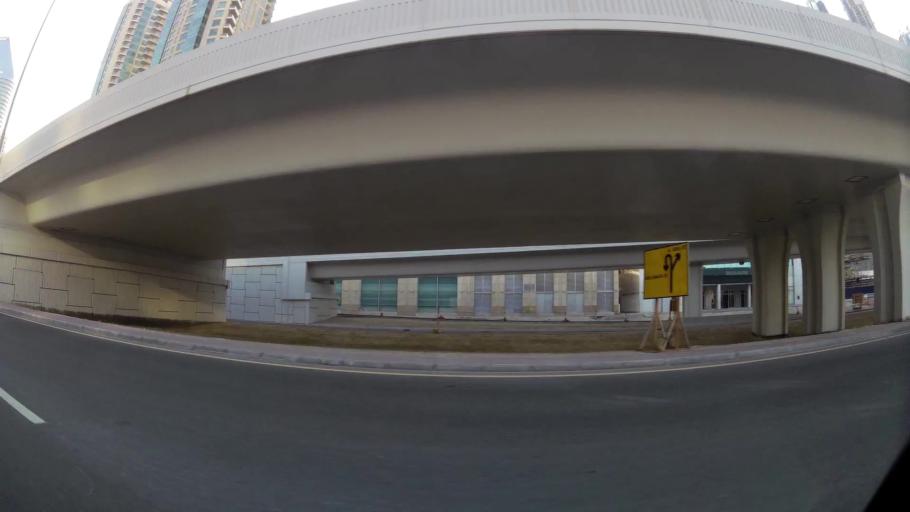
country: AE
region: Dubai
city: Dubai
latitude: 25.1908
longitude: 55.2828
